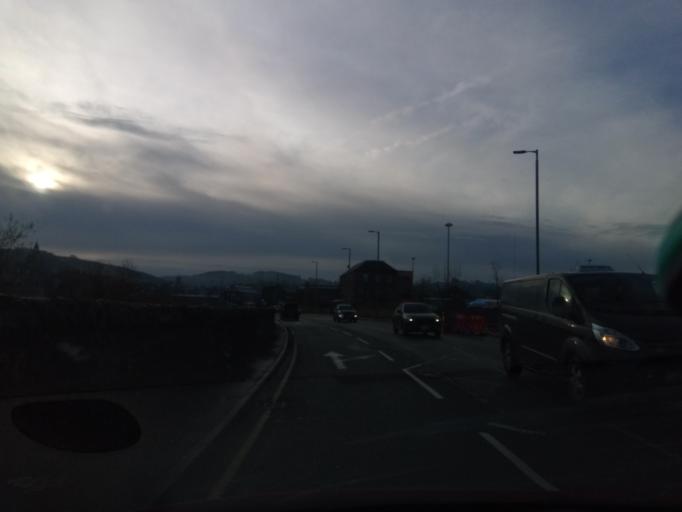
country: GB
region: Scotland
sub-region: The Scottish Borders
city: Hawick
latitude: 55.4263
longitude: -2.7876
